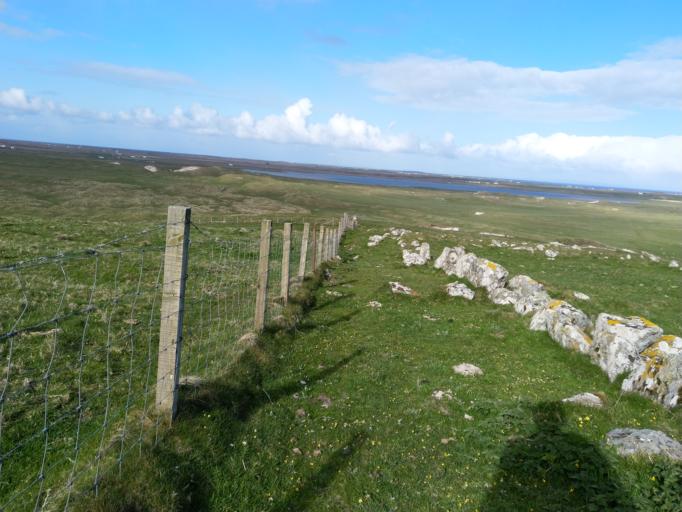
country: GB
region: Scotland
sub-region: Eilean Siar
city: Barra
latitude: 56.4624
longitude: -6.9679
